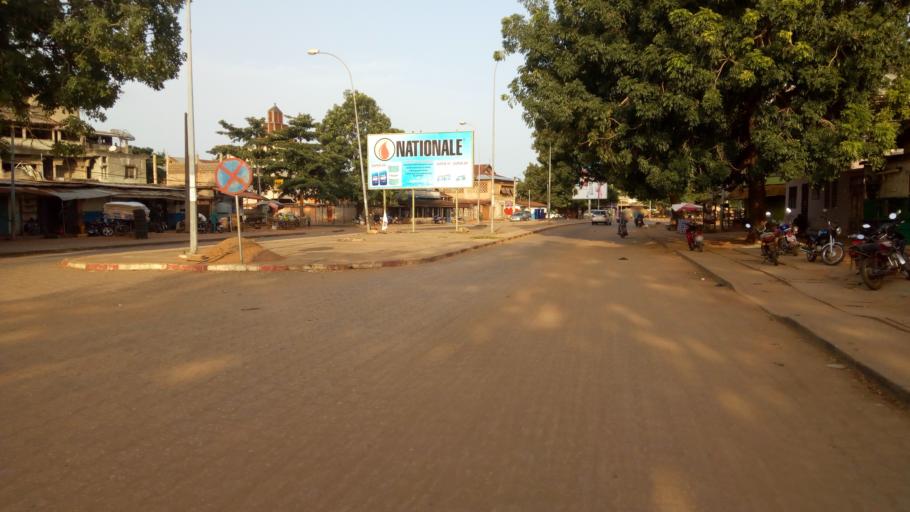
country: BJ
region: Queme
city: Porto-Novo
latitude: 6.4850
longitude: 2.6256
